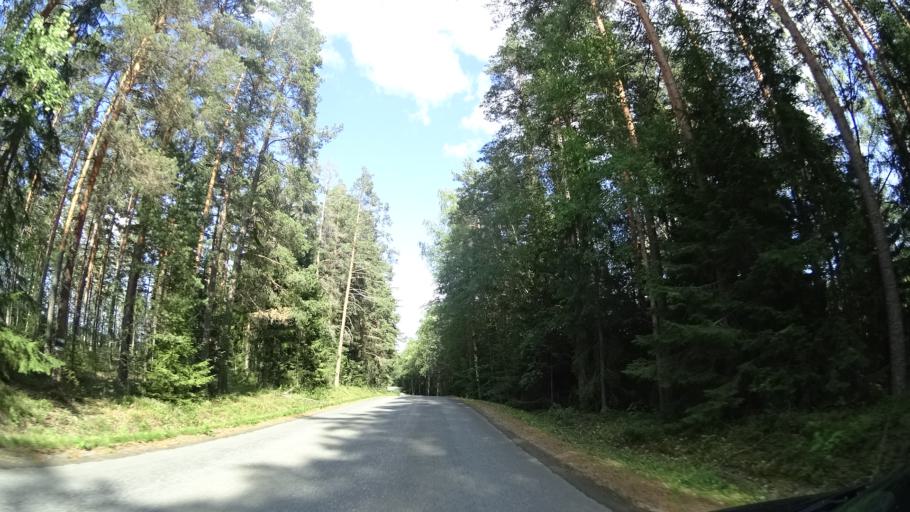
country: FI
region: Uusimaa
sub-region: Helsinki
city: Kaerkoelae
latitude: 60.7396
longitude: 24.1019
